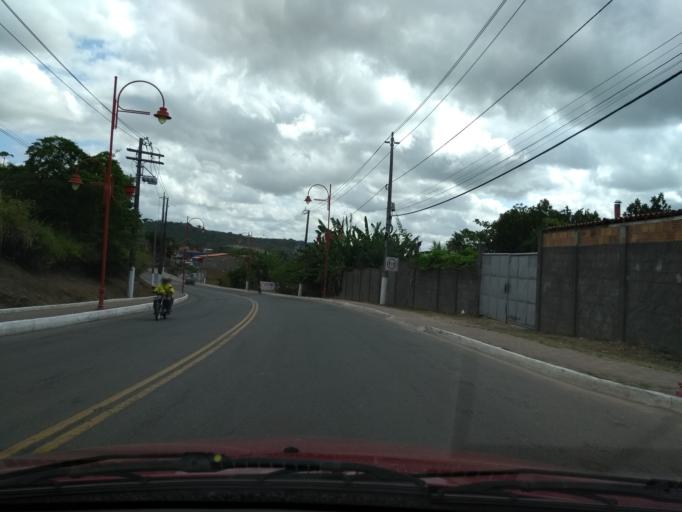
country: BR
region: Bahia
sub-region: Sao Francisco Do Conde
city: Sao Francisco do Conde
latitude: -12.6230
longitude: -38.6730
